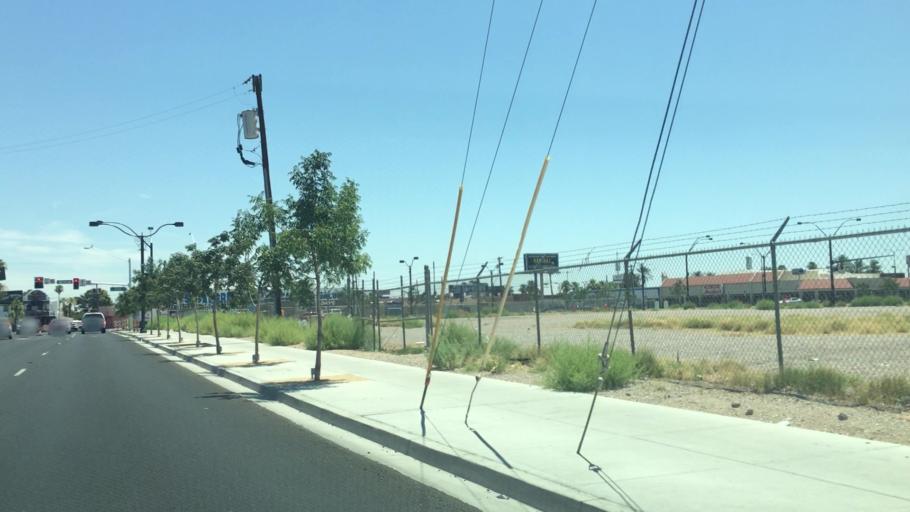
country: US
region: Nevada
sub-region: Clark County
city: Las Vegas
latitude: 36.1522
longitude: -115.1554
